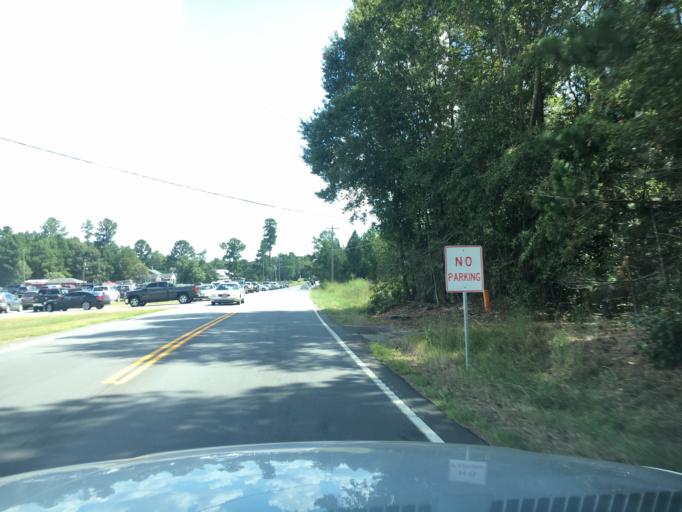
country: US
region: South Carolina
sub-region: Greenwood County
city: Ware Shoals
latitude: 34.5186
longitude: -82.1876
